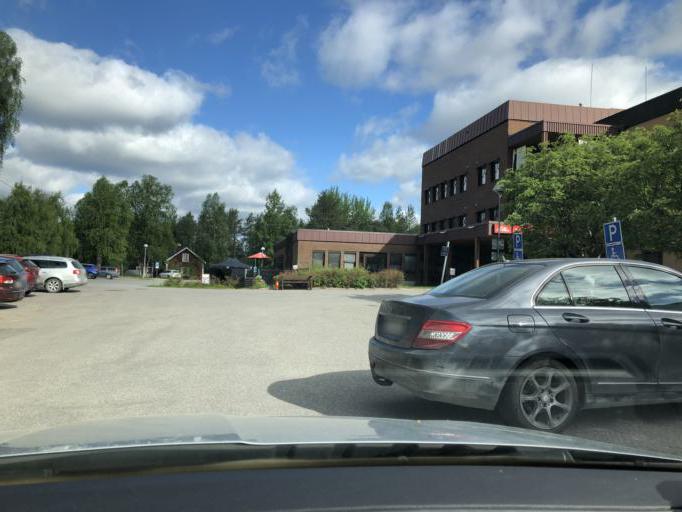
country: SE
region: Norrbotten
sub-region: Pajala Kommun
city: Pajala
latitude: 67.2231
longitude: 23.3429
